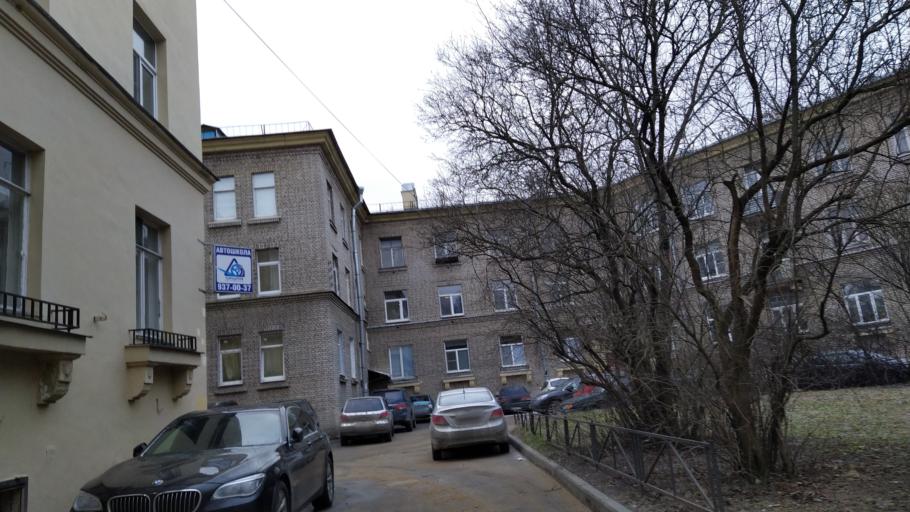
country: RU
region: St.-Petersburg
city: Pushkin
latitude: 59.7214
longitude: 30.4285
